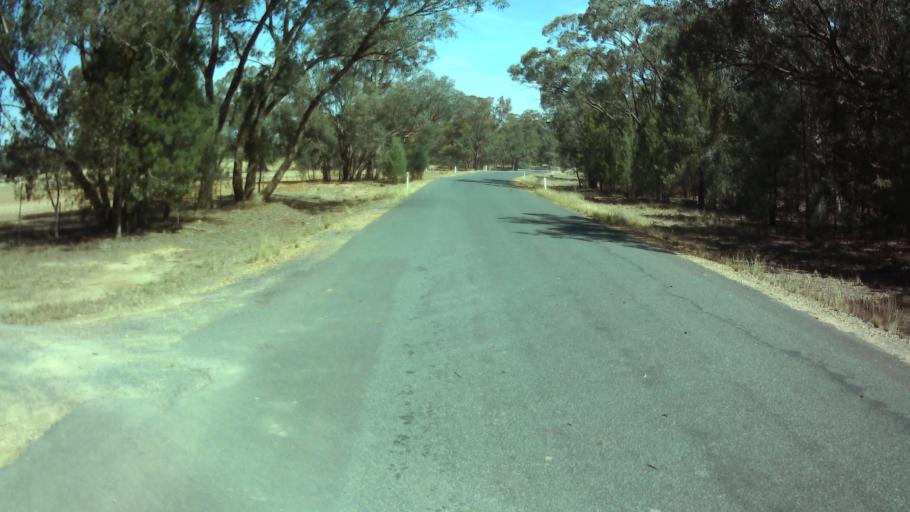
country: AU
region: New South Wales
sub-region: Weddin
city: Grenfell
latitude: -34.0252
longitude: 148.1318
